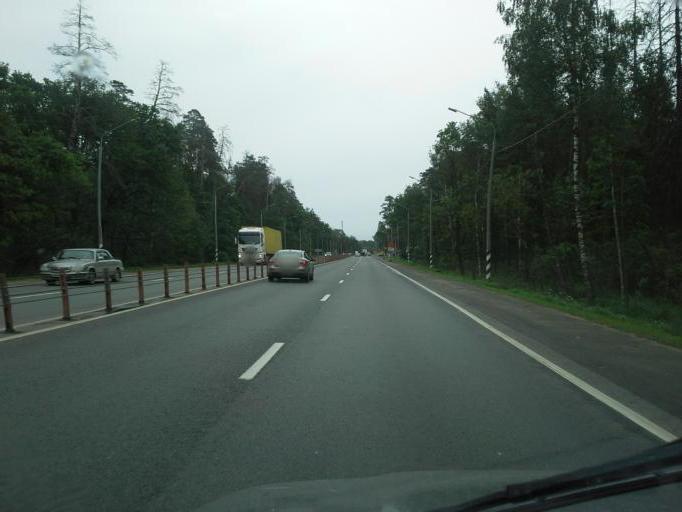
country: RU
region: Moskovskaya
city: Malaya Dubna
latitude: 55.8962
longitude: 39.0440
